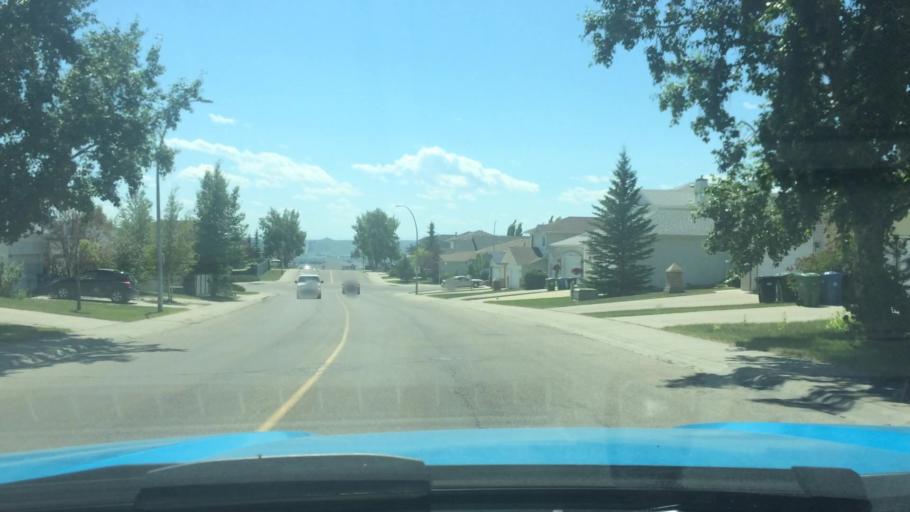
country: CA
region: Alberta
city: Calgary
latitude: 51.1363
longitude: -114.1914
